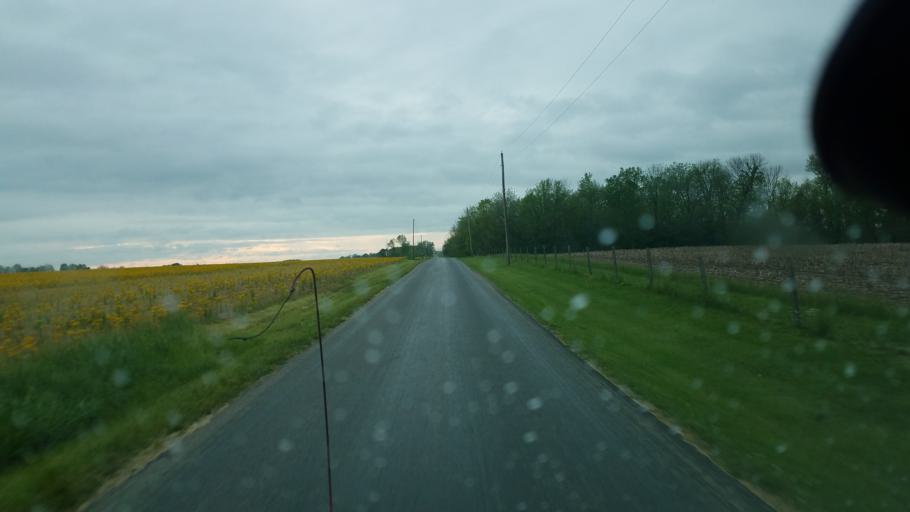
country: US
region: Ohio
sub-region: Highland County
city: Greenfield
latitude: 39.3213
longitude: -83.4216
